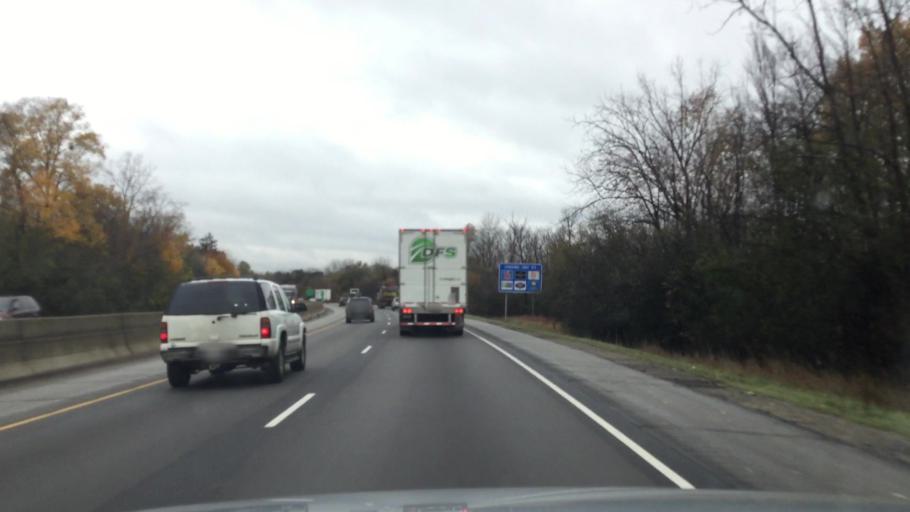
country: US
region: Michigan
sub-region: Washtenaw County
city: Ann Arbor
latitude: 42.2371
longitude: -83.7105
